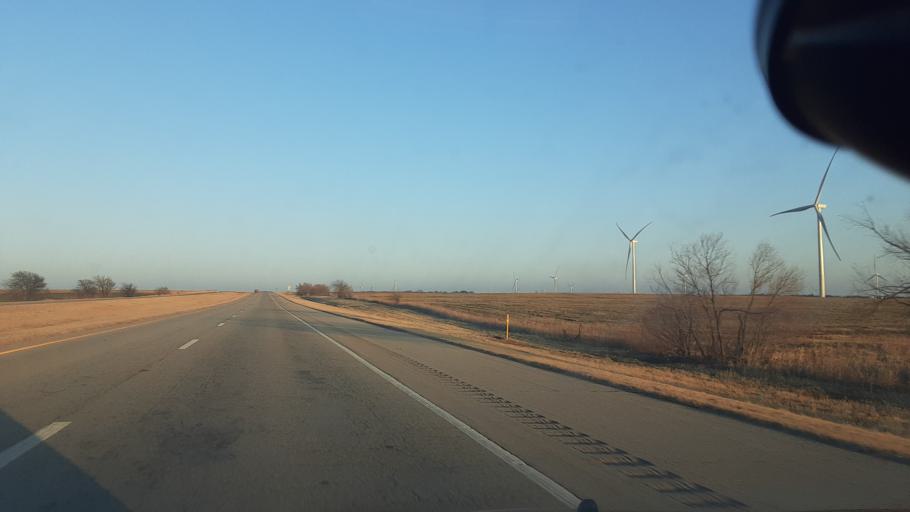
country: US
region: Oklahoma
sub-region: Noble County
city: Perry
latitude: 36.3976
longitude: -97.4588
